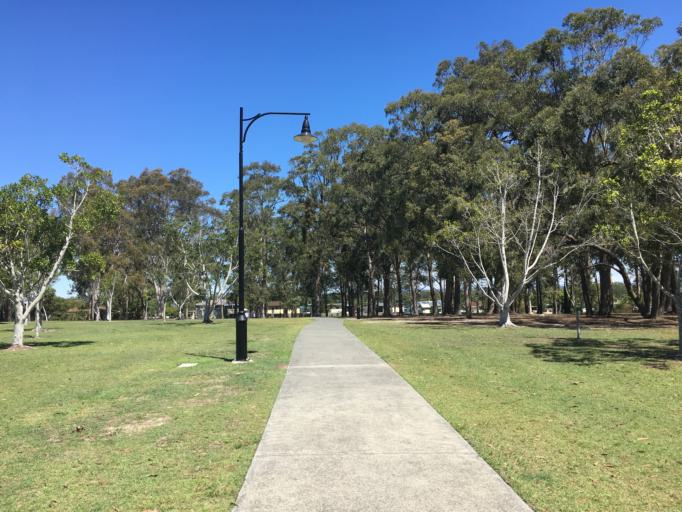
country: AU
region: Queensland
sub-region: Logan
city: Logan City
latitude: -27.6477
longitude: 153.1028
